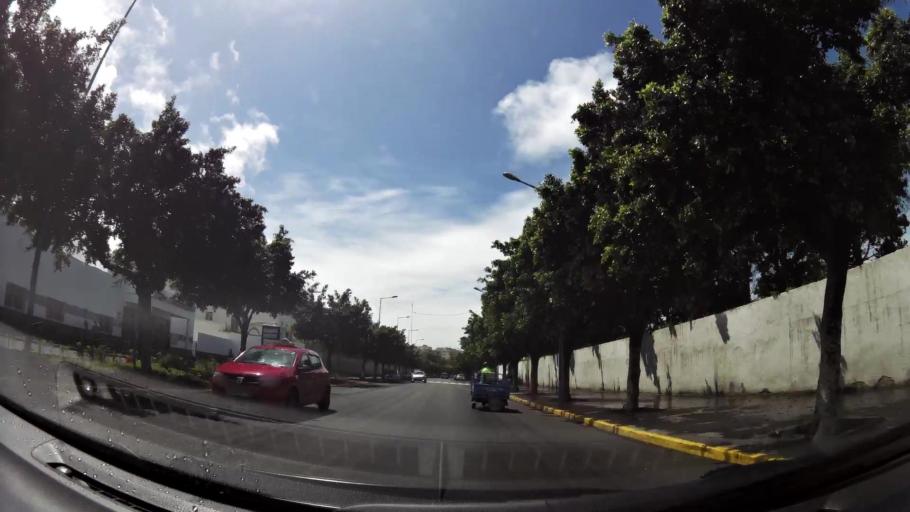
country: MA
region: Grand Casablanca
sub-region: Casablanca
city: Casablanca
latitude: 33.5761
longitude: -7.6200
